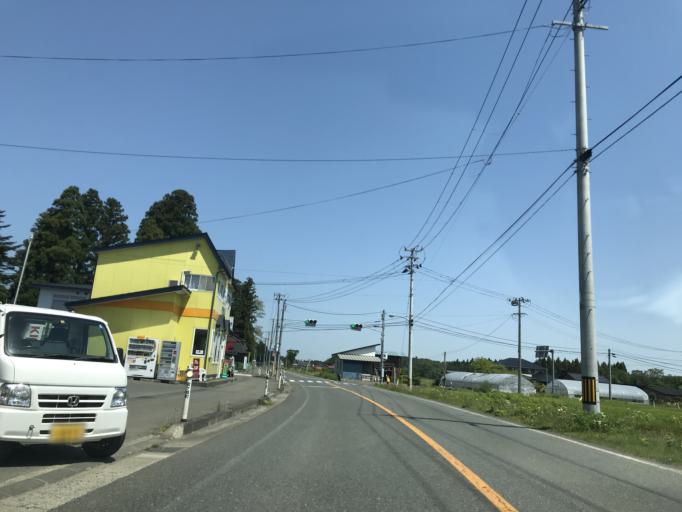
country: JP
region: Iwate
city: Kitakami
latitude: 39.2241
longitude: 141.0665
